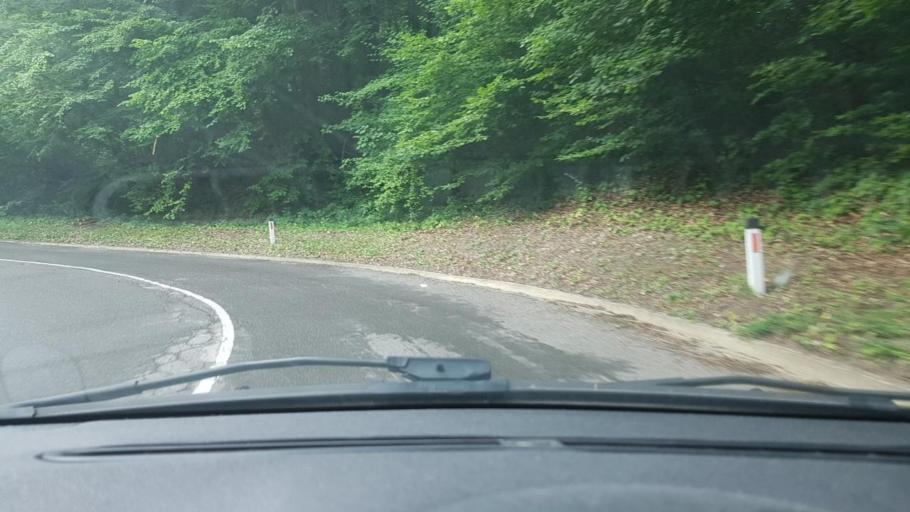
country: AT
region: Styria
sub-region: Politischer Bezirk Suedoststeiermark
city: Mureck
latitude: 46.7016
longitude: 15.7836
